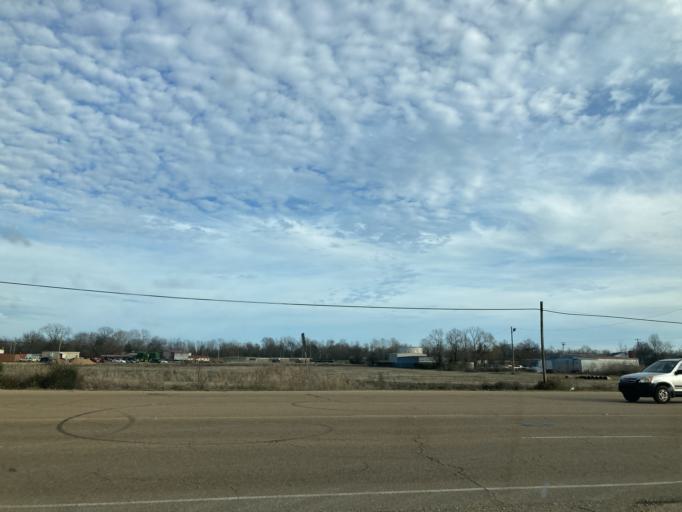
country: US
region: Mississippi
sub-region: Humphreys County
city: Belzoni
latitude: 33.1691
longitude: -90.4987
